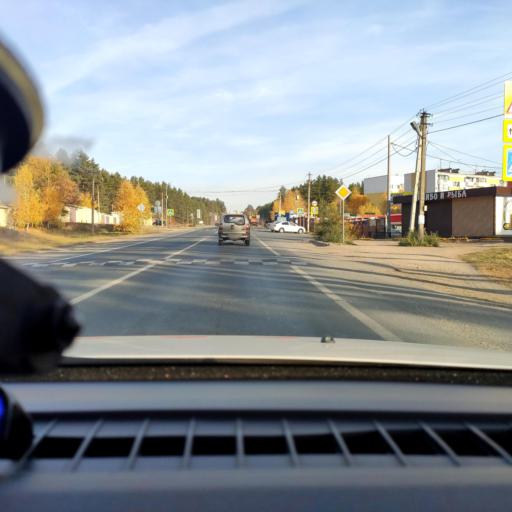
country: RU
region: Samara
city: Volzhskiy
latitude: 53.4376
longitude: 50.1246
